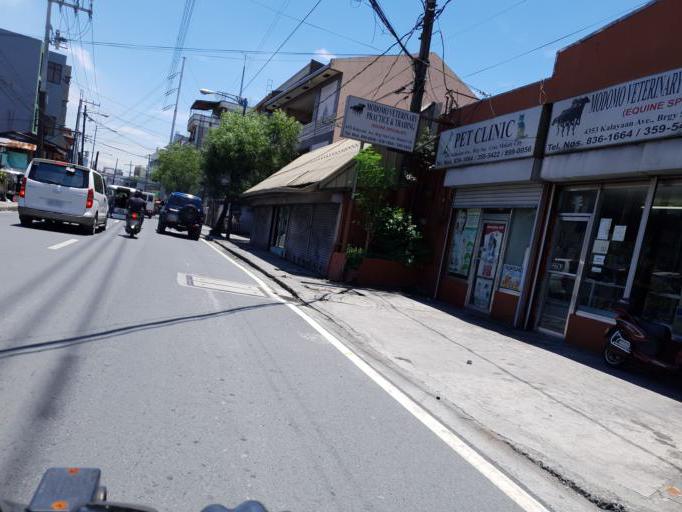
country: PH
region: Metro Manila
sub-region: Makati City
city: Makati City
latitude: 14.5702
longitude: 121.0153
